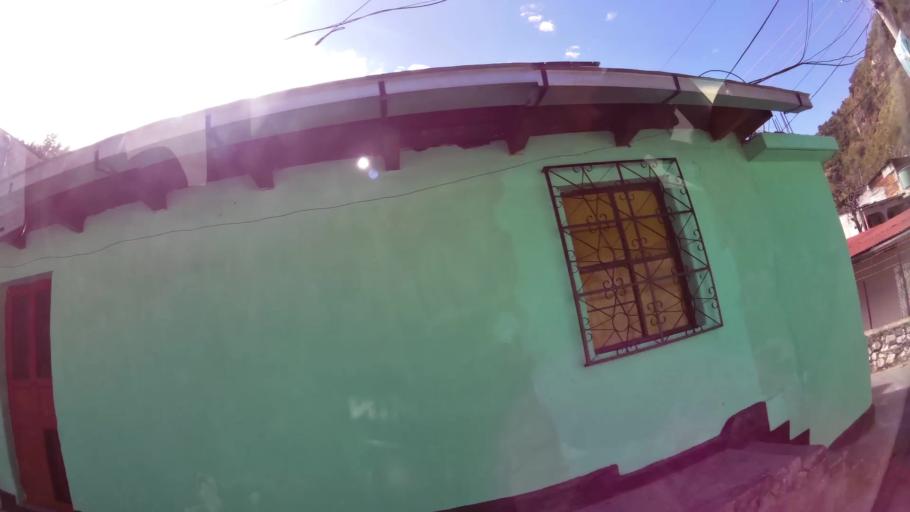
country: GT
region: Solola
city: Panajachel
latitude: 14.7461
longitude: -91.1548
